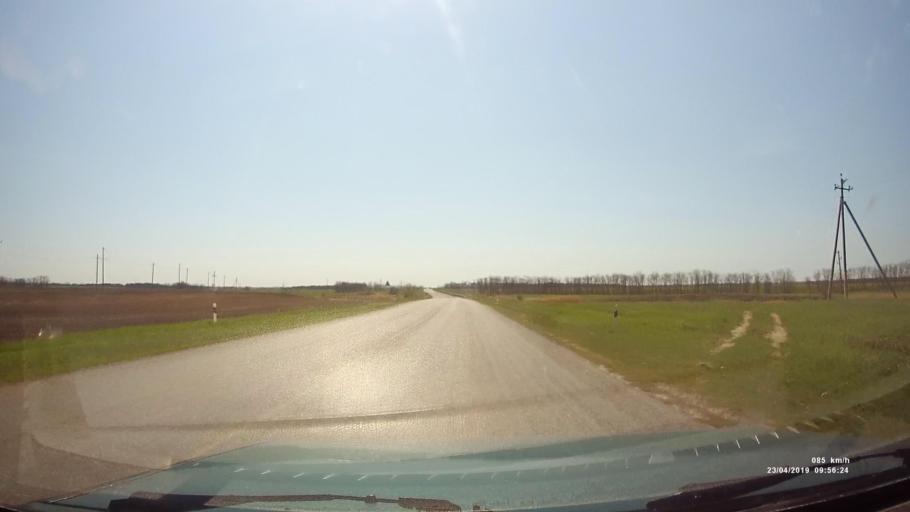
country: RU
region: Rostov
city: Orlovskiy
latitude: 46.7983
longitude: 42.0724
